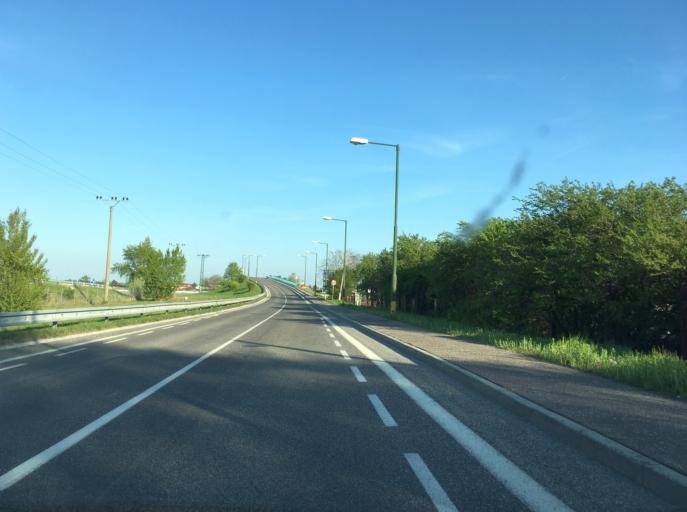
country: AT
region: Burgenland
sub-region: Politischer Bezirk Neusiedl am See
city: Kittsee
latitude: 48.0708
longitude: 17.0985
